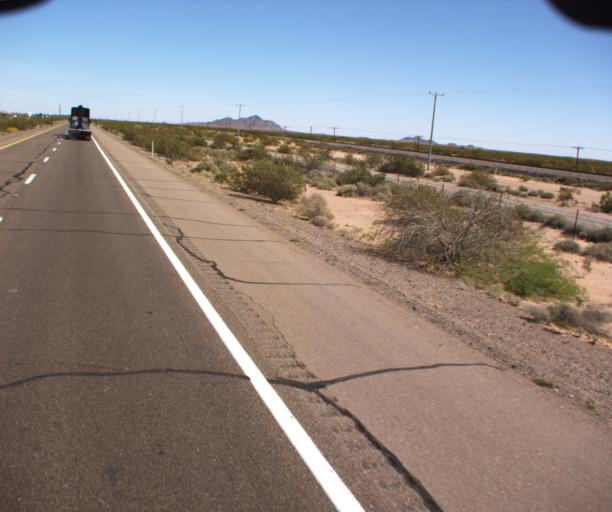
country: US
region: Arizona
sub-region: Yuma County
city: Wellton
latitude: 32.7837
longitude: -113.5747
